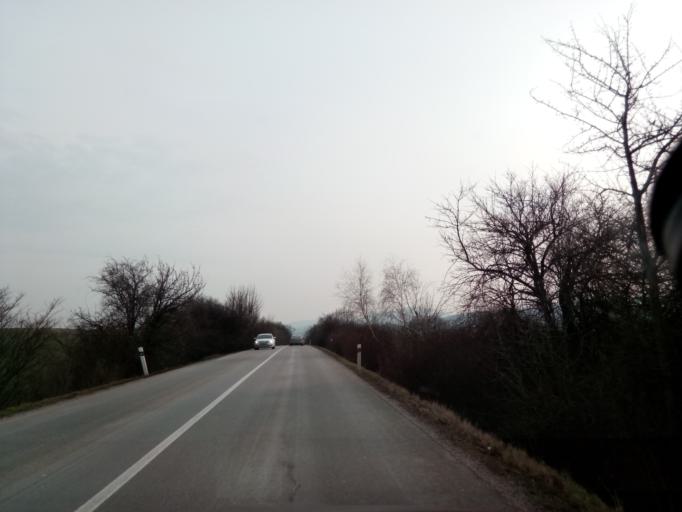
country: SK
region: Kosicky
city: Secovce
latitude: 48.6328
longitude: 21.5546
